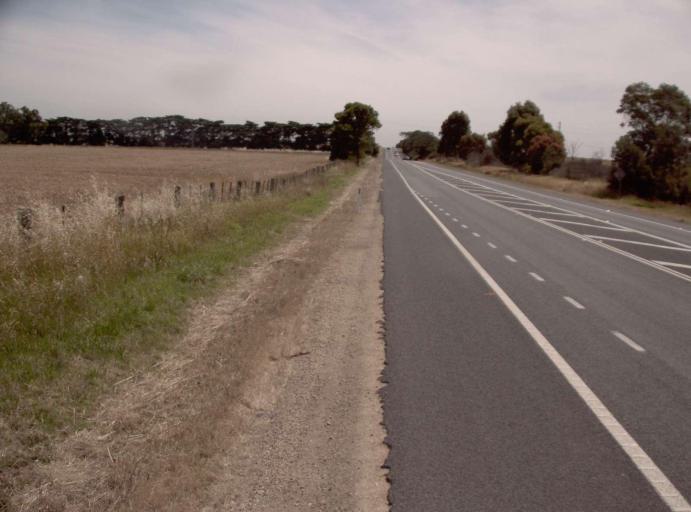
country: AU
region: Victoria
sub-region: Wellington
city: Heyfield
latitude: -38.1201
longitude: 146.8580
